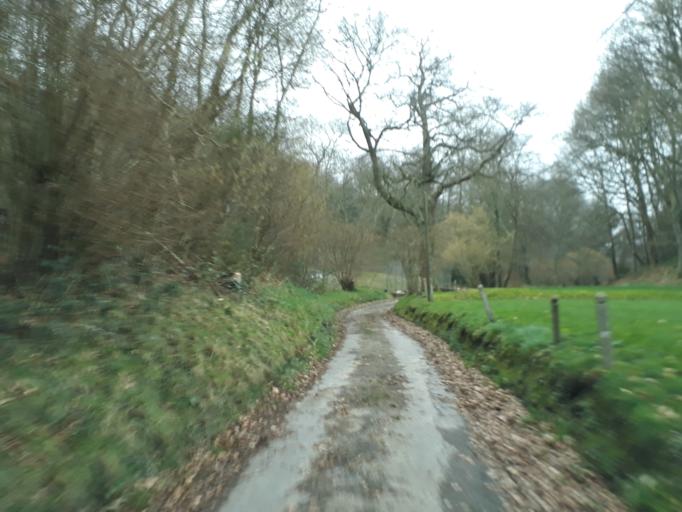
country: FR
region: Haute-Normandie
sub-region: Departement de la Seine-Maritime
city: Yport
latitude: 49.7303
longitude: 0.2958
